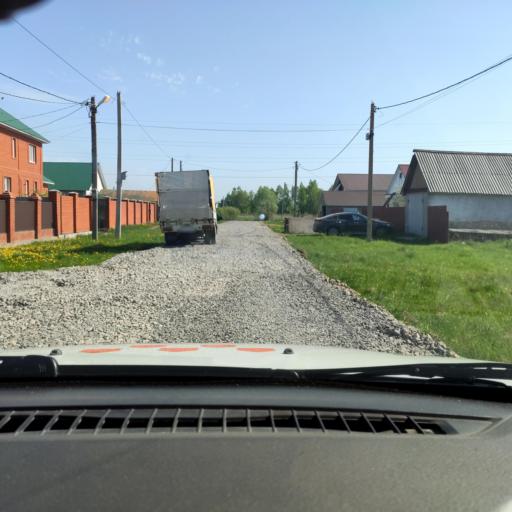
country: RU
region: Bashkortostan
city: Mikhaylovka
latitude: 54.7831
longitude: 55.8225
